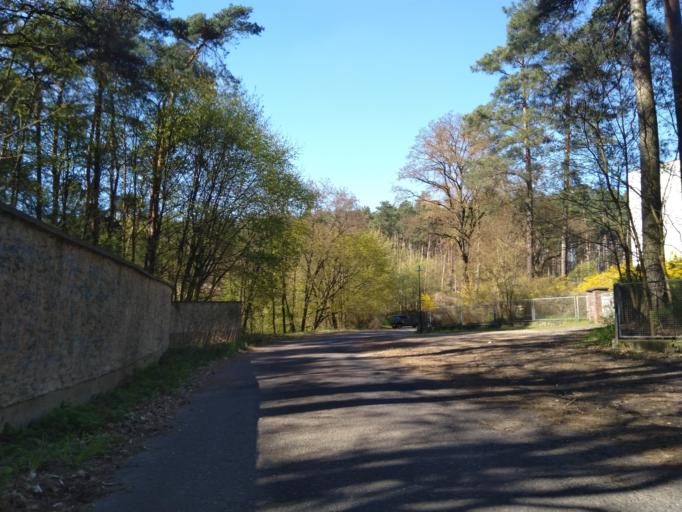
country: DE
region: Brandenburg
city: Biesenthal
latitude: 52.7737
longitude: 13.6017
